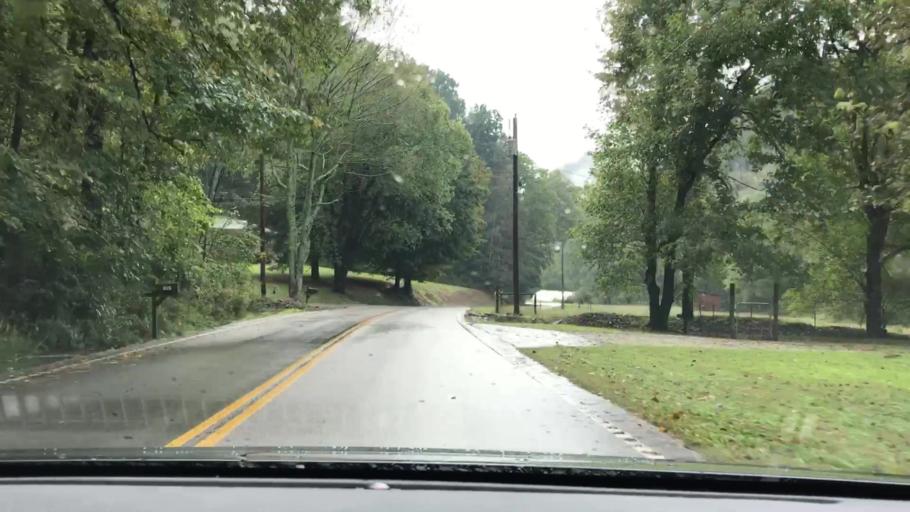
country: US
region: Tennessee
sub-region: Macon County
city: Red Boiling Springs
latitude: 36.4198
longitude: -85.9259
